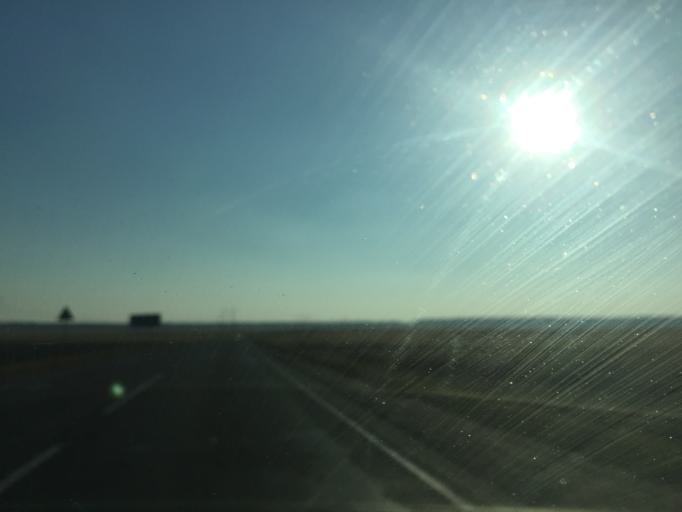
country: BY
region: Gomel
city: Dobrush
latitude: 52.3837
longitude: 31.2660
